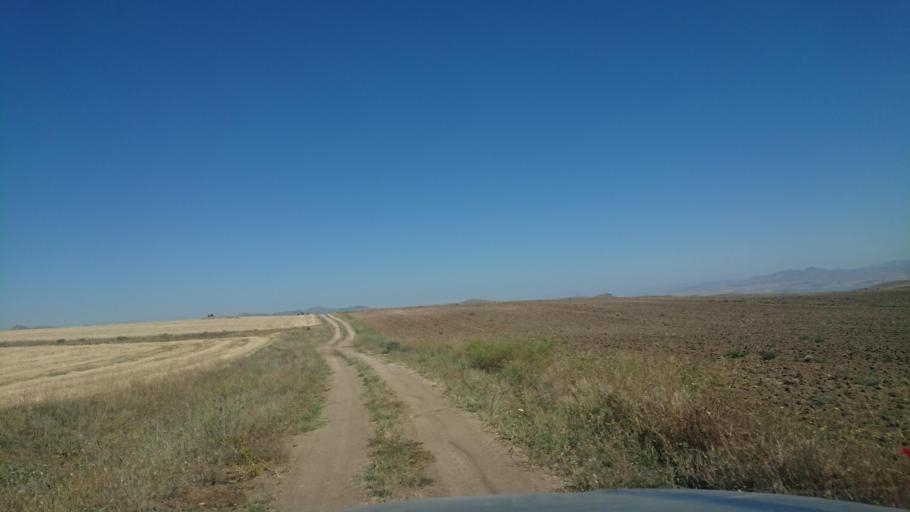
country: TR
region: Aksaray
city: Sariyahsi
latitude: 38.9336
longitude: 33.8442
